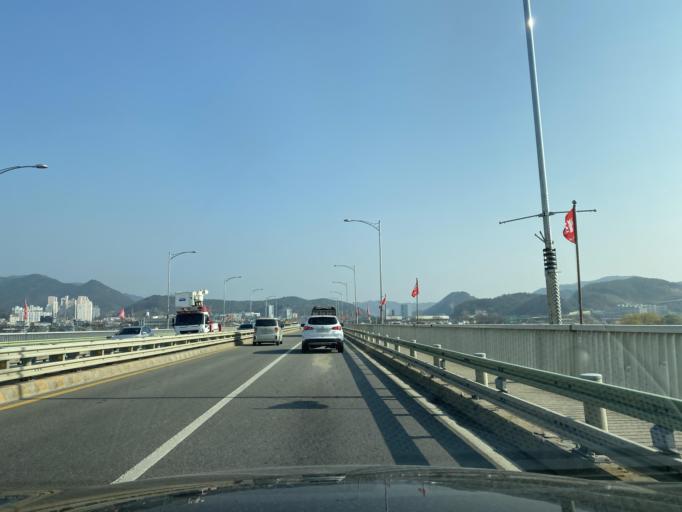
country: KR
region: Chungcheongnam-do
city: Yesan
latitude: 36.6844
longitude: 126.8193
